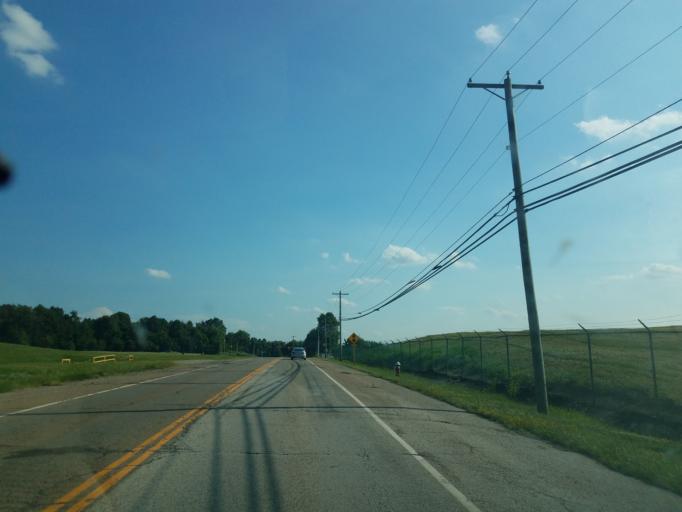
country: US
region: Ohio
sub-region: Summit County
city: Greensburg
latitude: 40.9018
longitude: -81.4395
